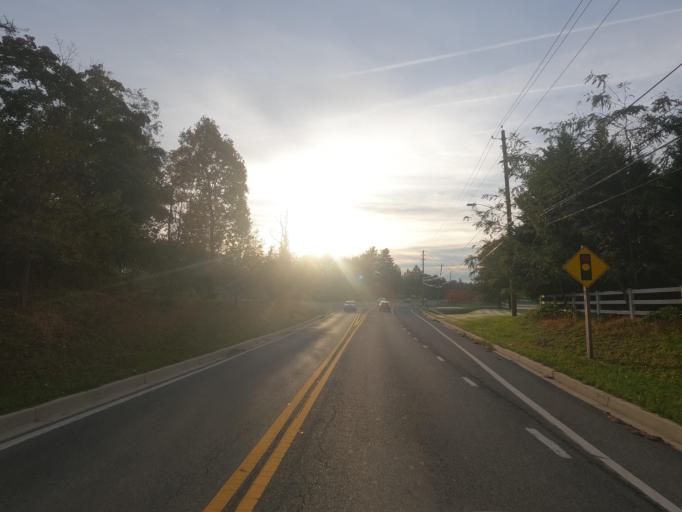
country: US
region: Maryland
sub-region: Montgomery County
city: Ashton-Sandy Spring
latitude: 39.1395
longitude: -77.0347
